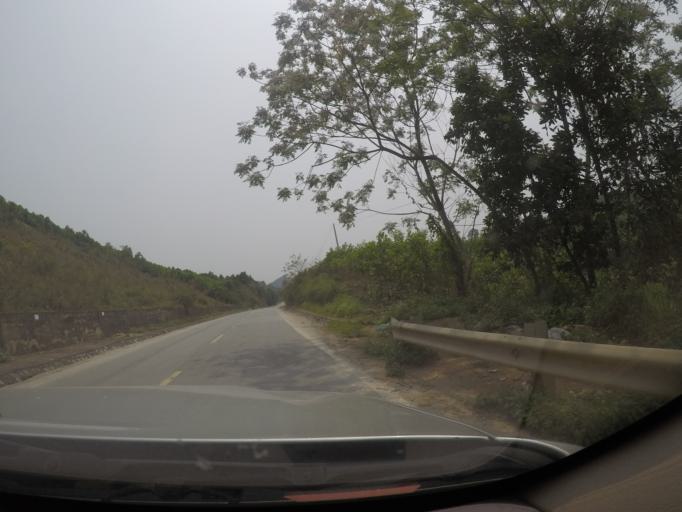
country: VN
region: Thanh Hoa
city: Thi Tran Yen Cat
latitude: 19.6885
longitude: 105.4549
